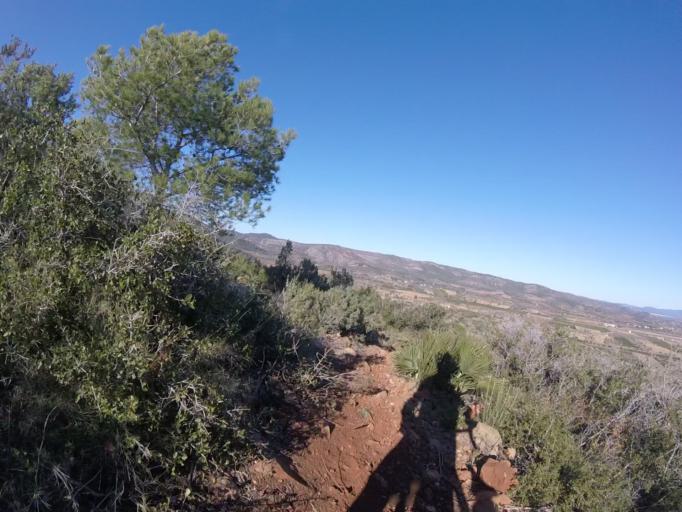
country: ES
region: Valencia
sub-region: Provincia de Castello
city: Orpesa/Oropesa del Mar
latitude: 40.1202
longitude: 0.1214
